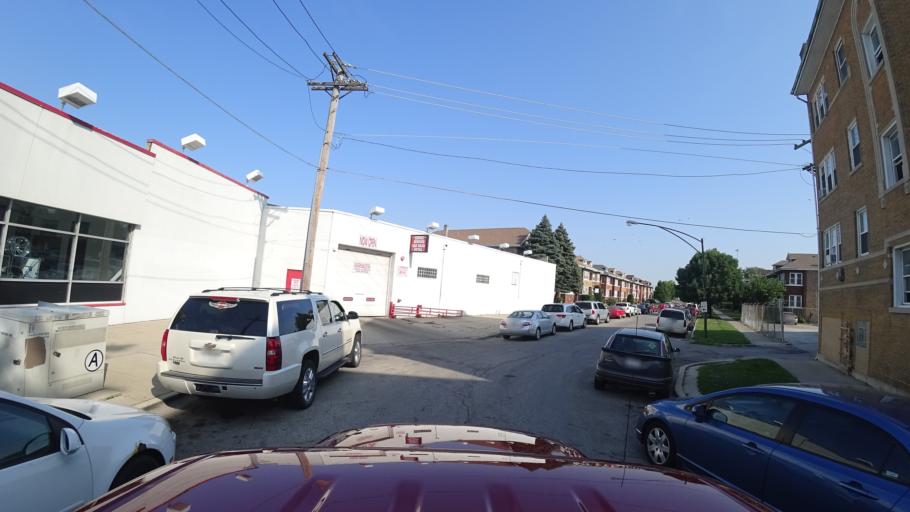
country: US
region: Illinois
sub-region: Cook County
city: Cicero
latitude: 41.8137
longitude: -87.7054
